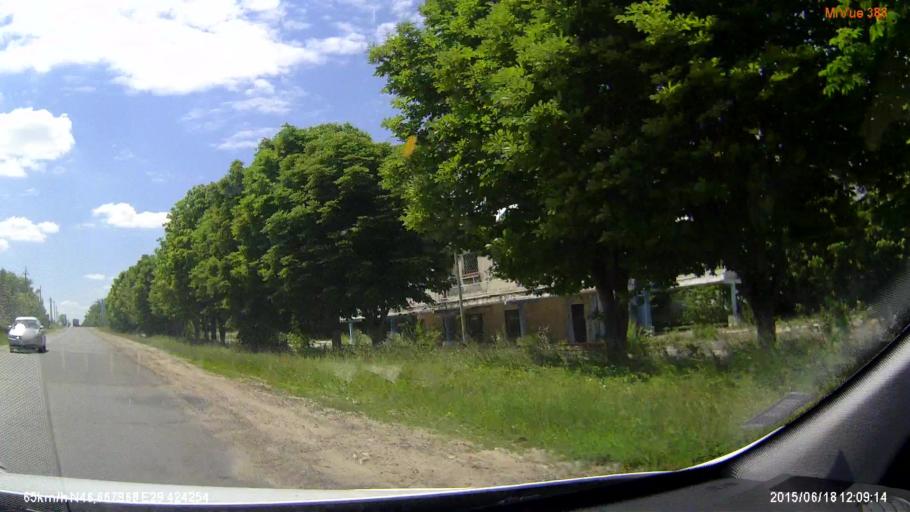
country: MD
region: Causeni
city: Causeni
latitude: 46.6681
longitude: 29.4247
